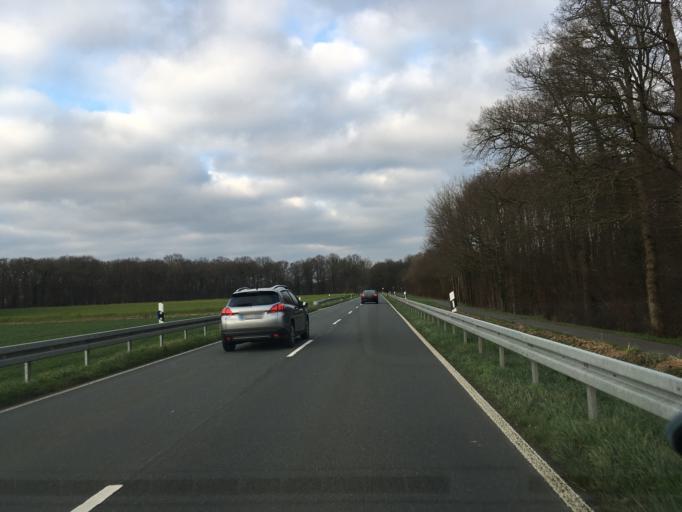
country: DE
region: North Rhine-Westphalia
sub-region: Regierungsbezirk Munster
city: Ahaus
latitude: 52.1440
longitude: 6.9889
